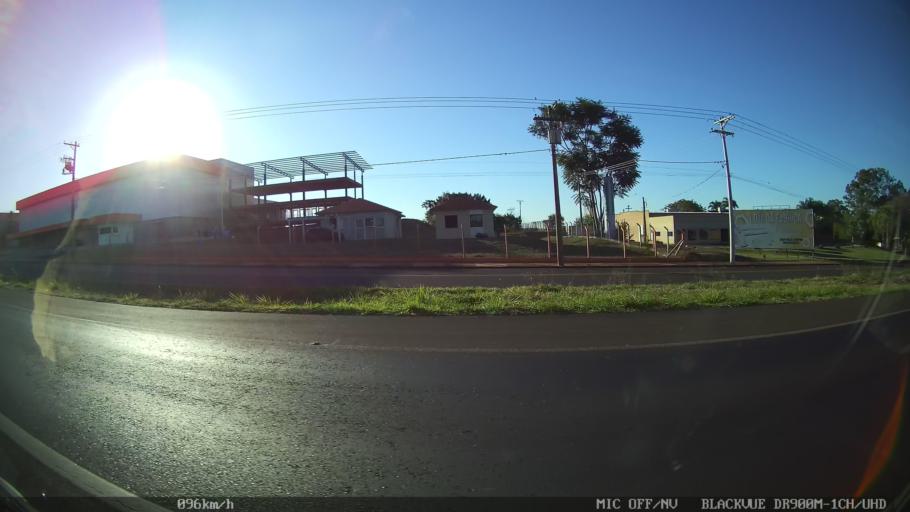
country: BR
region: Sao Paulo
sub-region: Guapiacu
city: Guapiacu
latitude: -20.7848
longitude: -49.2732
